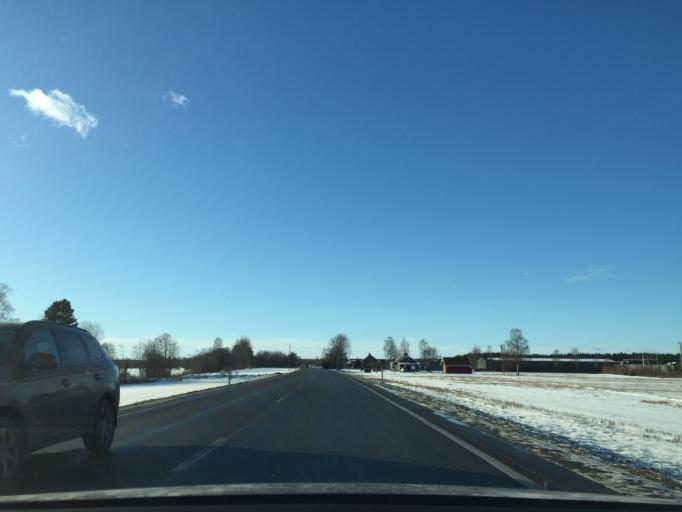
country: NO
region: Hedmark
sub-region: Sor-Odal
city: Skarnes
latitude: 60.2073
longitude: 11.6023
